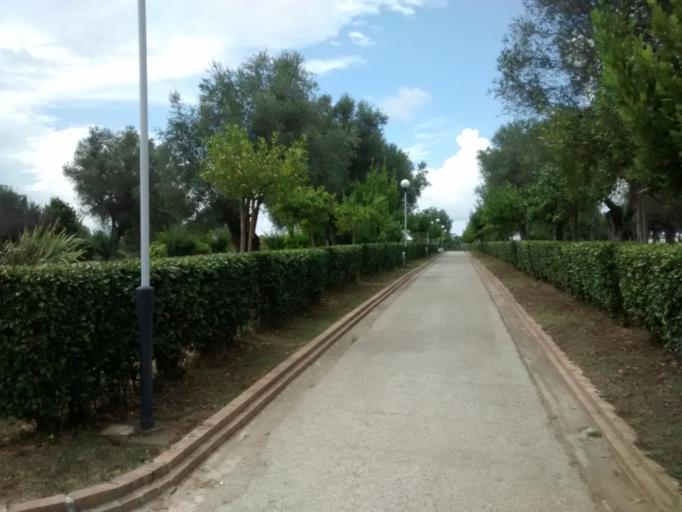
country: IT
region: Calabria
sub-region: Provincia di Vibo-Valentia
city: Vibo Valentia
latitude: 38.6642
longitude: 16.0799
